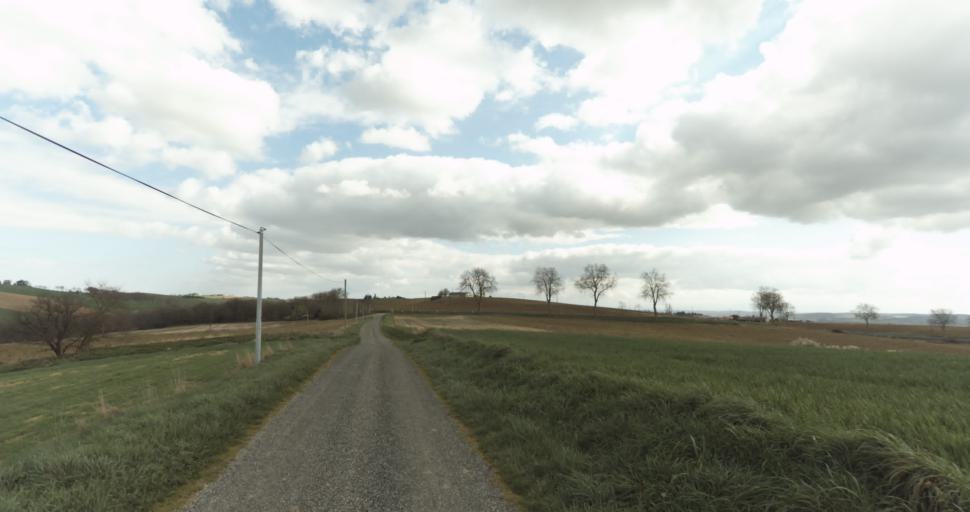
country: FR
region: Midi-Pyrenees
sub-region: Departement de la Haute-Garonne
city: Auterive
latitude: 43.3612
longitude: 1.4961
